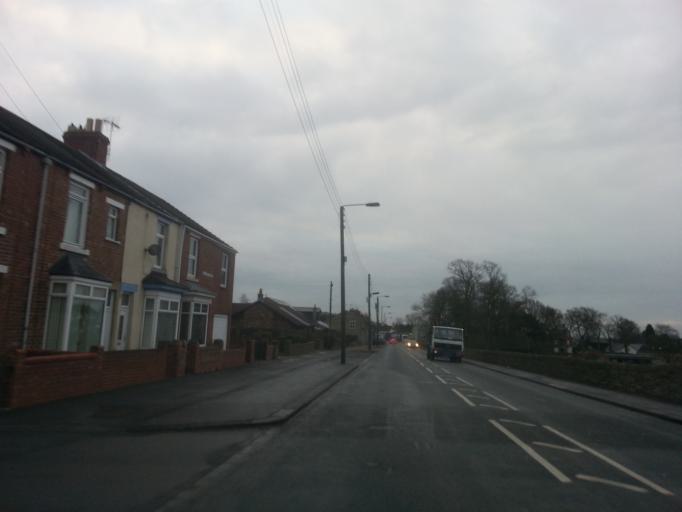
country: GB
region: England
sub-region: County Durham
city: Hamsterley
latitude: 54.7056
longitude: -1.7851
